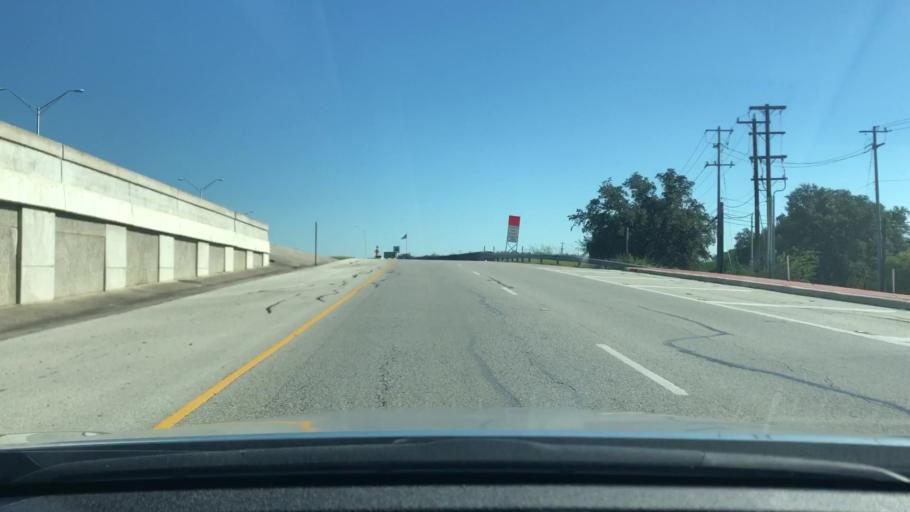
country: US
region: Texas
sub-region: Bexar County
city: Live Oak
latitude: 29.5495
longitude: -98.3201
